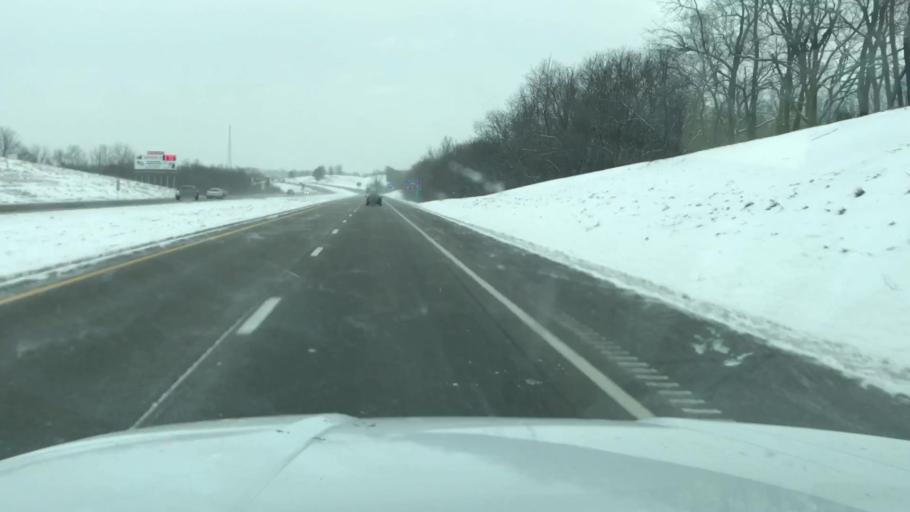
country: US
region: Missouri
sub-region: Andrew County
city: Country Club Village
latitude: 39.8268
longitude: -94.8055
